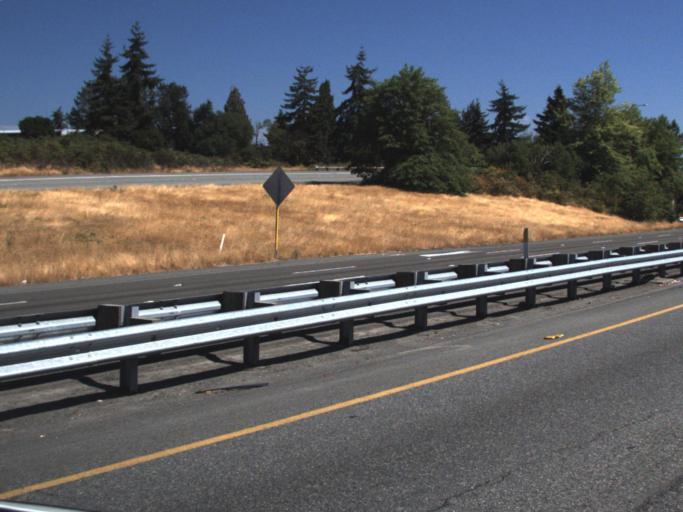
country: US
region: Washington
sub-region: King County
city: SeaTac
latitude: 47.4641
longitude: -122.2973
